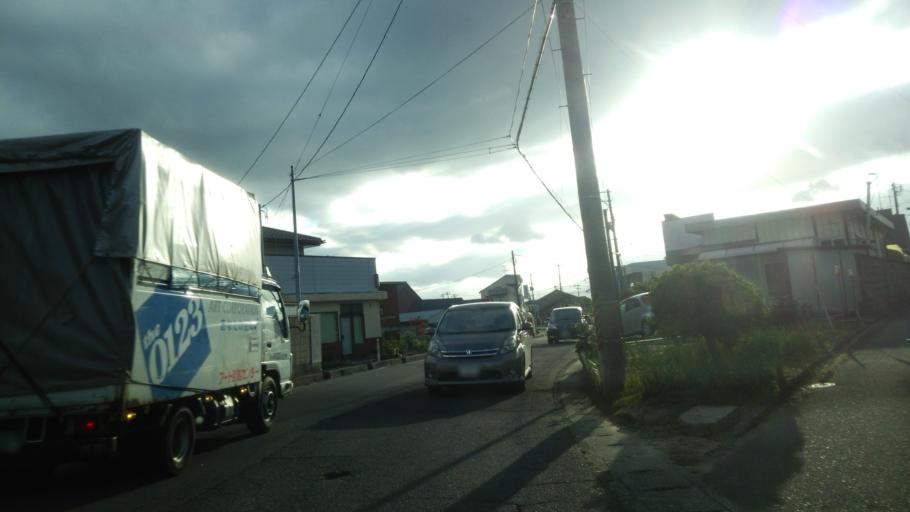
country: JP
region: Fukushima
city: Koriyama
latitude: 37.3779
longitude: 140.3443
